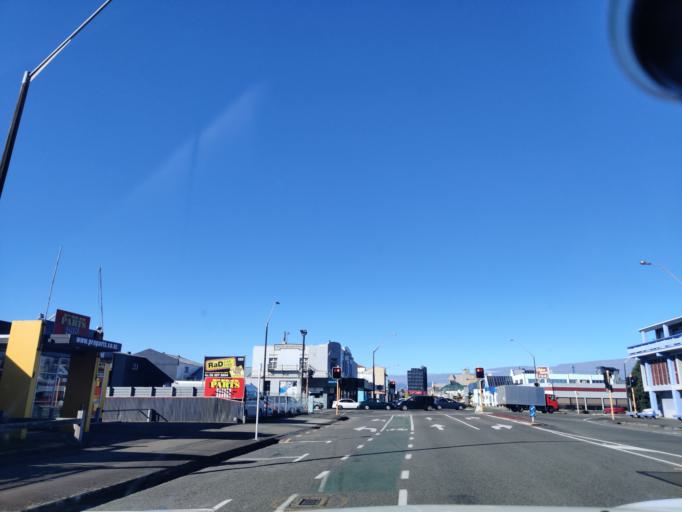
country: NZ
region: Manawatu-Wanganui
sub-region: Palmerston North City
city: Palmerston North
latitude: -40.3569
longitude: 175.6045
